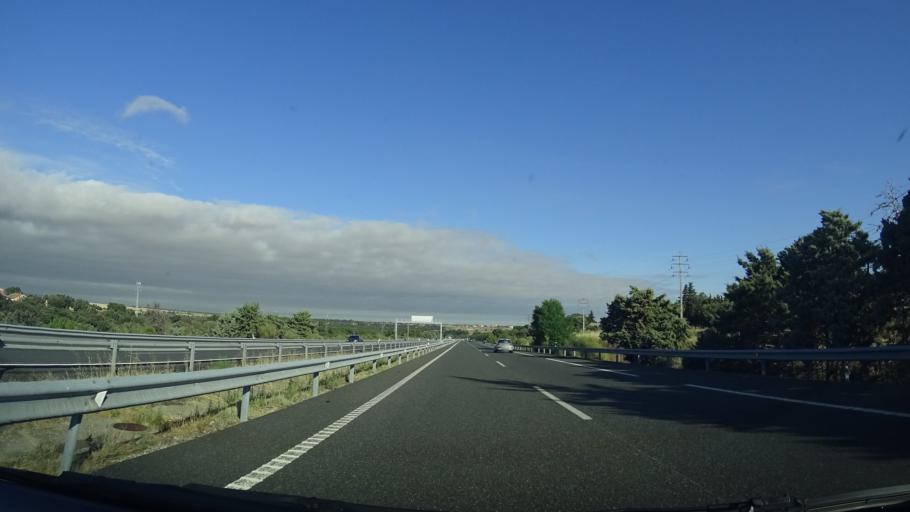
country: ES
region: Castille and Leon
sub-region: Provincia de Segovia
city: Labajos
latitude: 40.8568
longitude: -4.5499
